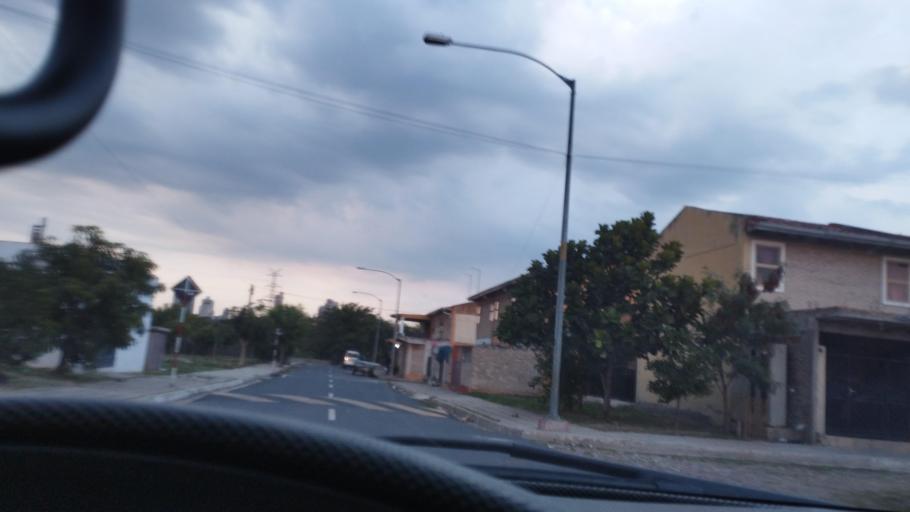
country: PY
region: Asuncion
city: Asuncion
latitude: -25.2730
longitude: -57.6145
